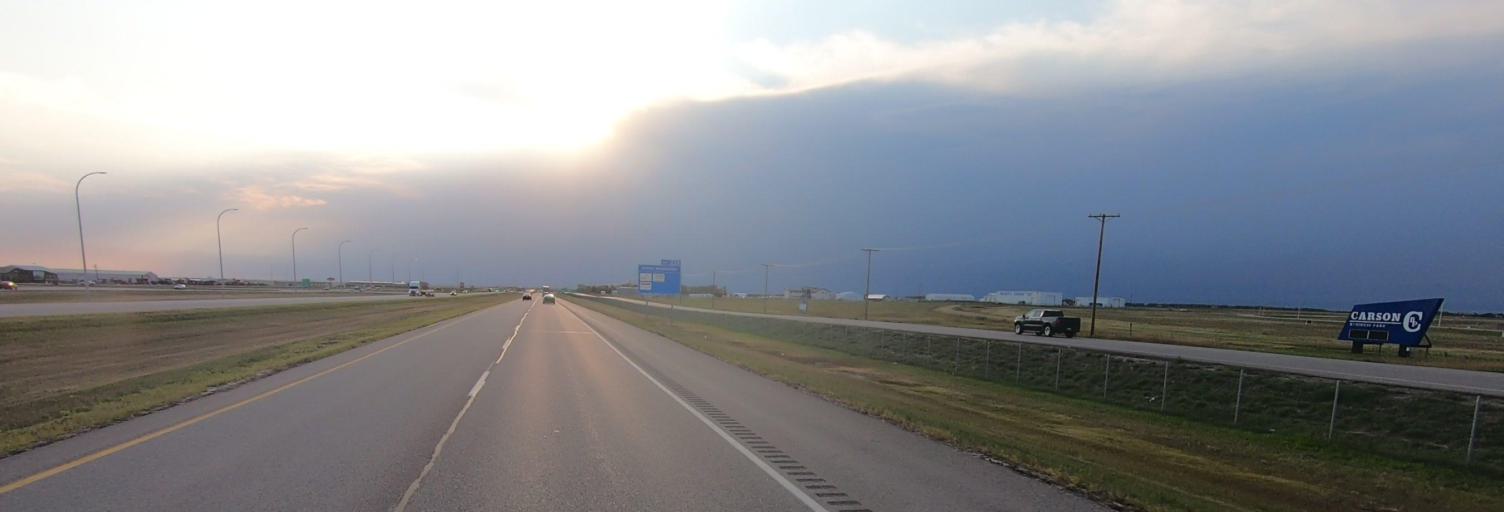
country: CA
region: Saskatchewan
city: Pilot Butte
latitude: 50.4505
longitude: -104.4056
